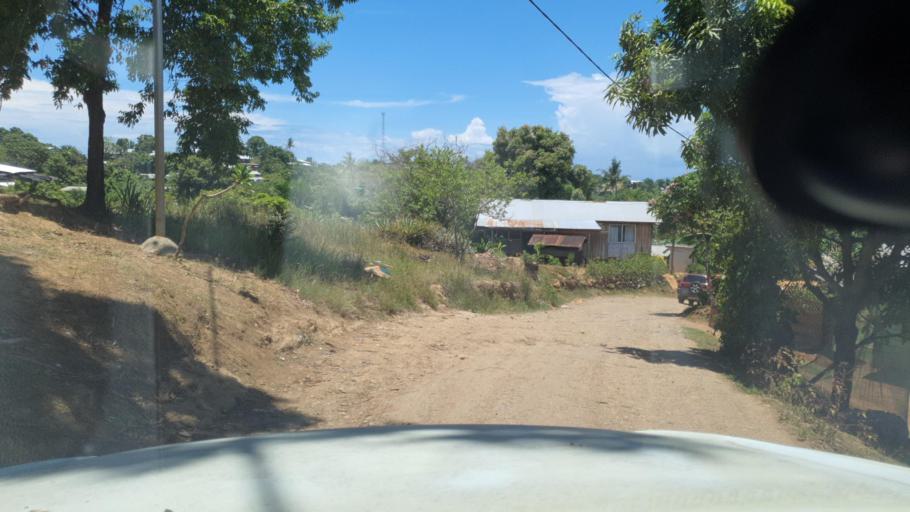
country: SB
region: Guadalcanal
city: Honiara
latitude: -9.4546
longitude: 159.9929
